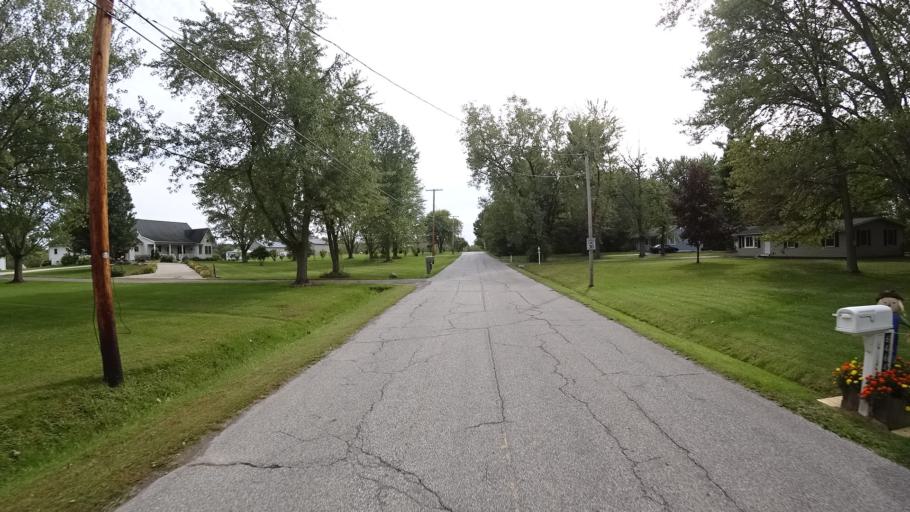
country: US
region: Indiana
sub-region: LaPorte County
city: Trail Creek
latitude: 41.7022
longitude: -86.8163
